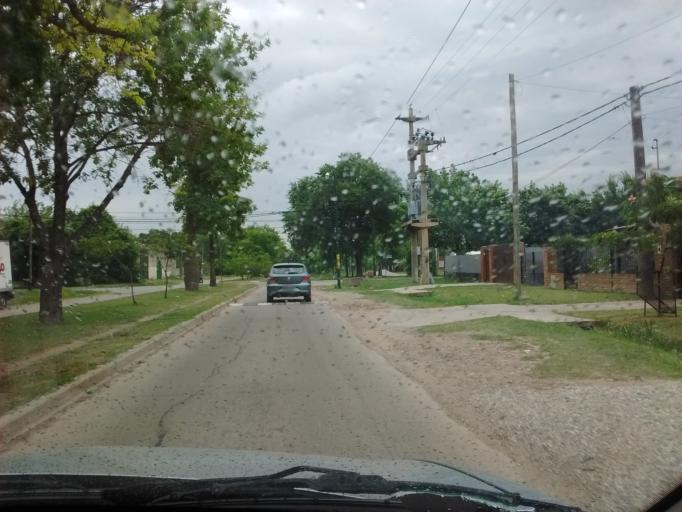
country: AR
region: Santa Fe
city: Funes
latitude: -32.9151
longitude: -60.7986
